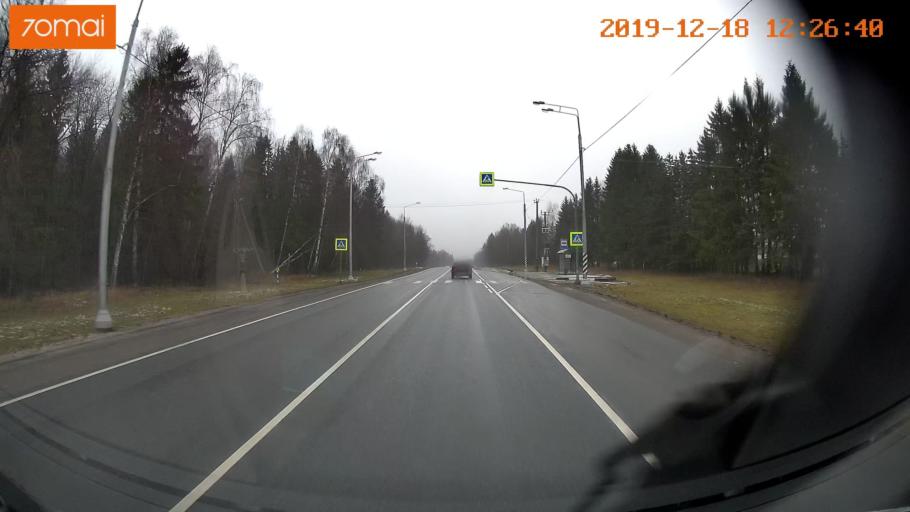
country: RU
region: Moskovskaya
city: Novopetrovskoye
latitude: 56.0536
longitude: 36.5017
